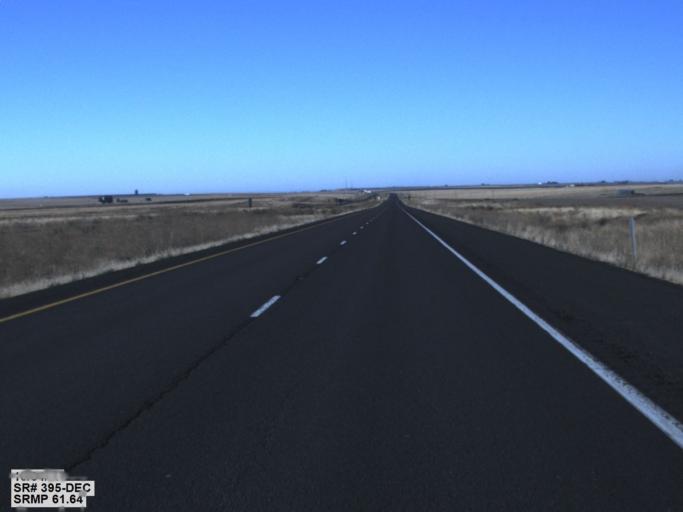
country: US
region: Washington
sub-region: Franklin County
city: Connell
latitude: 46.7401
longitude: -118.8143
